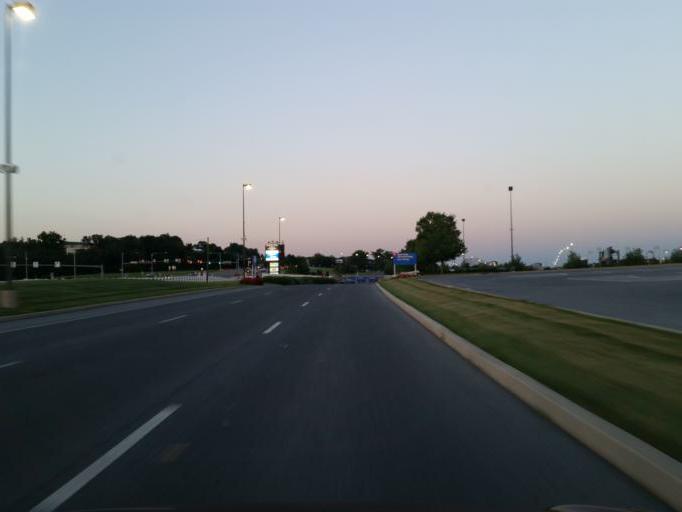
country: US
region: Pennsylvania
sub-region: Dauphin County
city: Hershey
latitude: 40.2880
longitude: -76.6712
